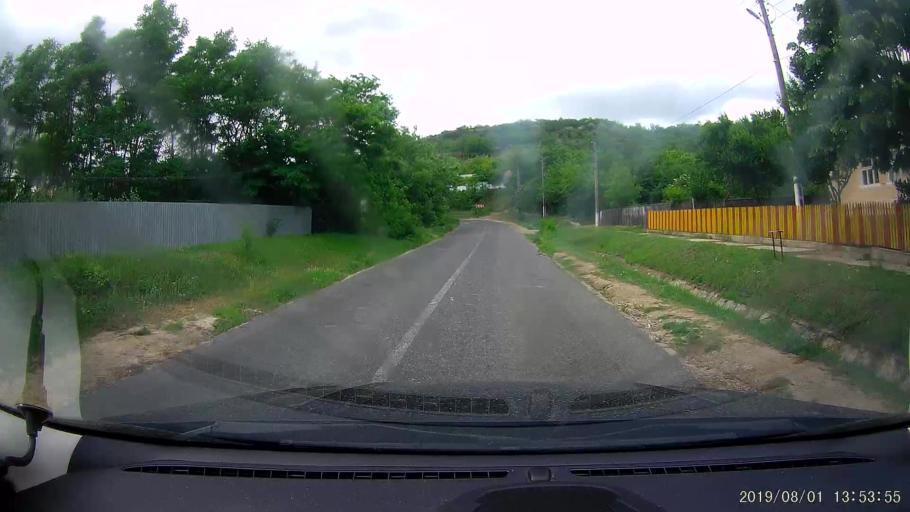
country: RO
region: Galati
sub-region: Comuna Vladesti
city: Vladesti
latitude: 45.8361
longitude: 28.0874
